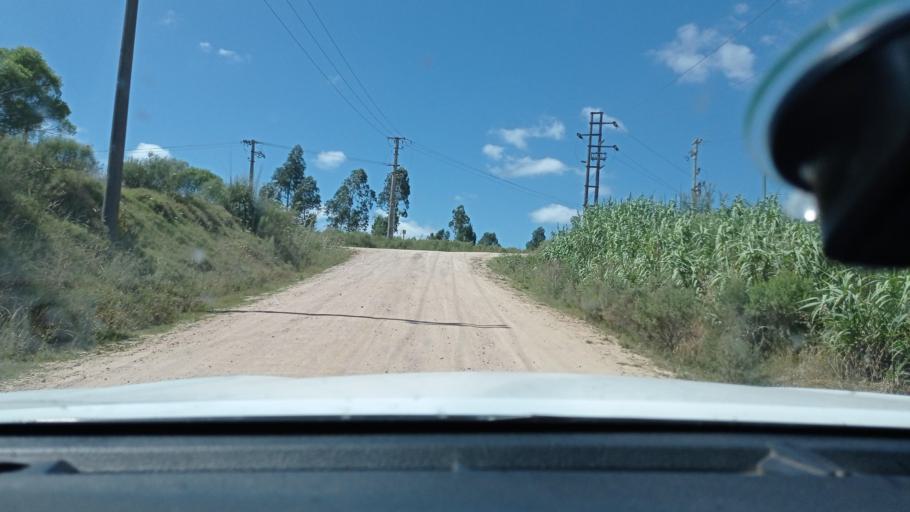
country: UY
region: Canelones
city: Pando
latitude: -34.7258
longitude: -55.9735
